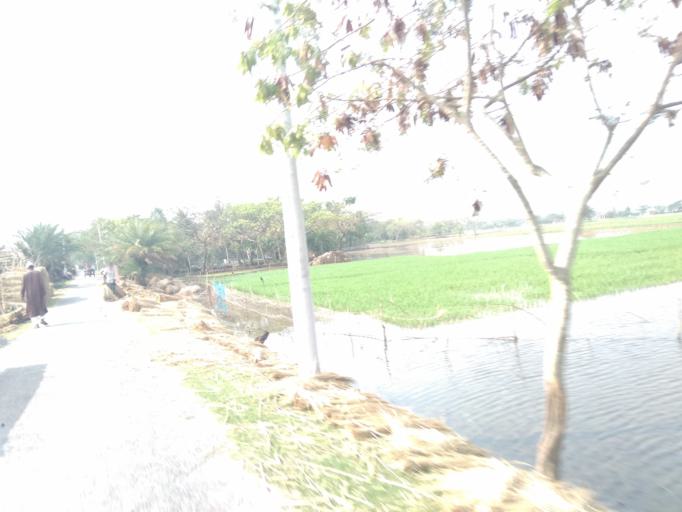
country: IN
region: West Bengal
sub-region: North 24 Parganas
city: Gosaba
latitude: 22.2582
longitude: 89.1151
